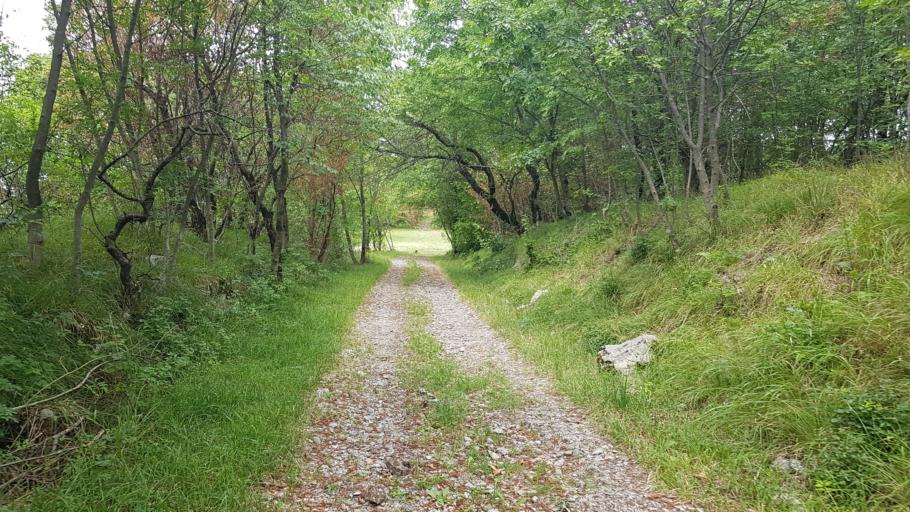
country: SI
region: Kanal
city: Deskle
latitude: 46.0149
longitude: 13.6352
